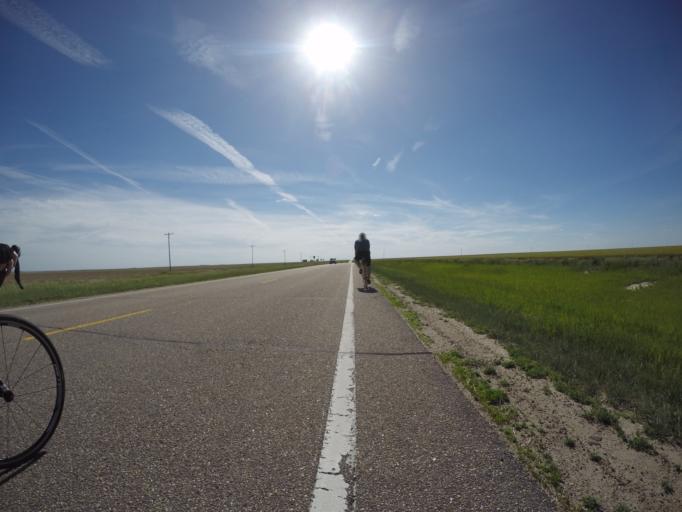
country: US
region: Kansas
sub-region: Cheyenne County
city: Saint Francis
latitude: 39.7567
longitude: -101.9711
